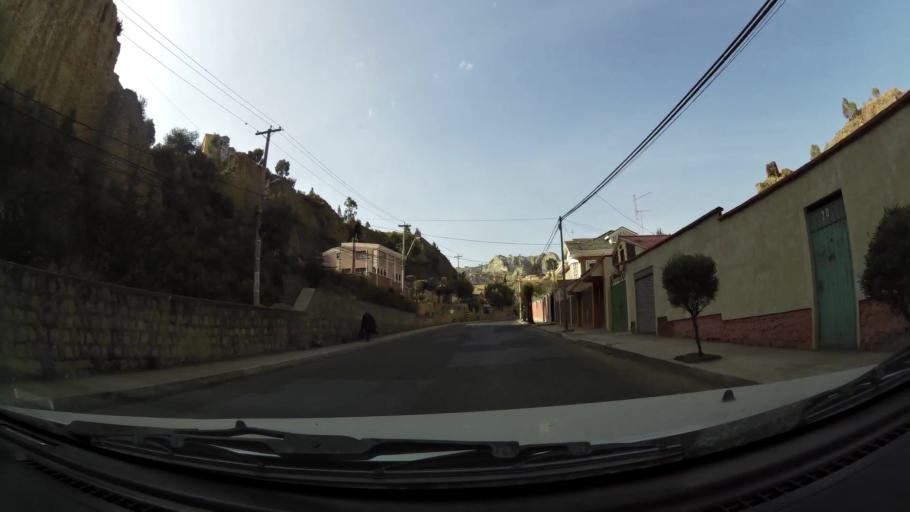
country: BO
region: La Paz
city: La Paz
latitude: -16.5315
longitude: -68.0801
